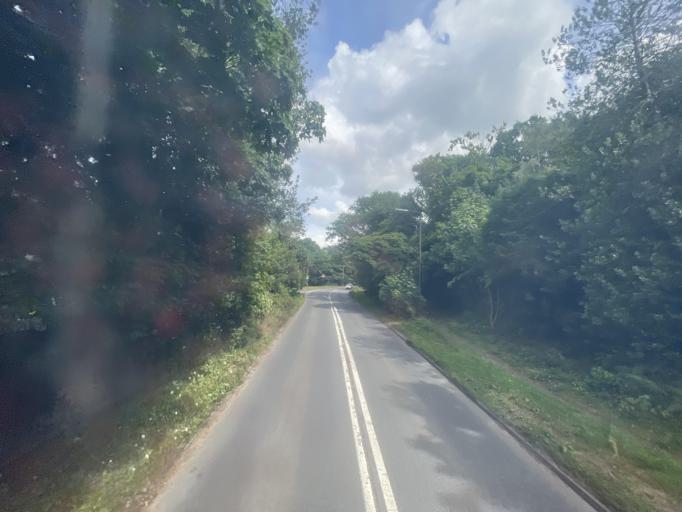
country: GB
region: England
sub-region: Greater London
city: West Wickham
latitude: 51.3696
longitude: 0.0090
